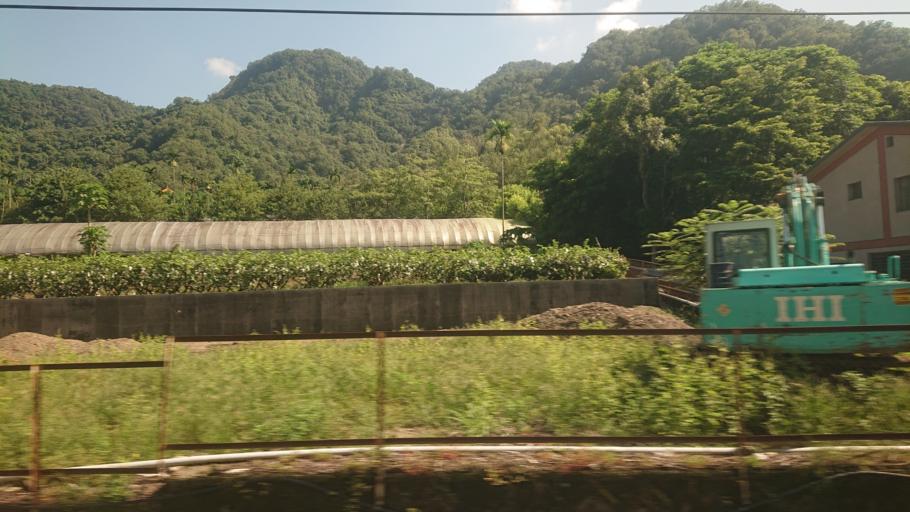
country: TW
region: Taiwan
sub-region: Nantou
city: Puli
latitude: 24.0608
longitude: 120.8988
